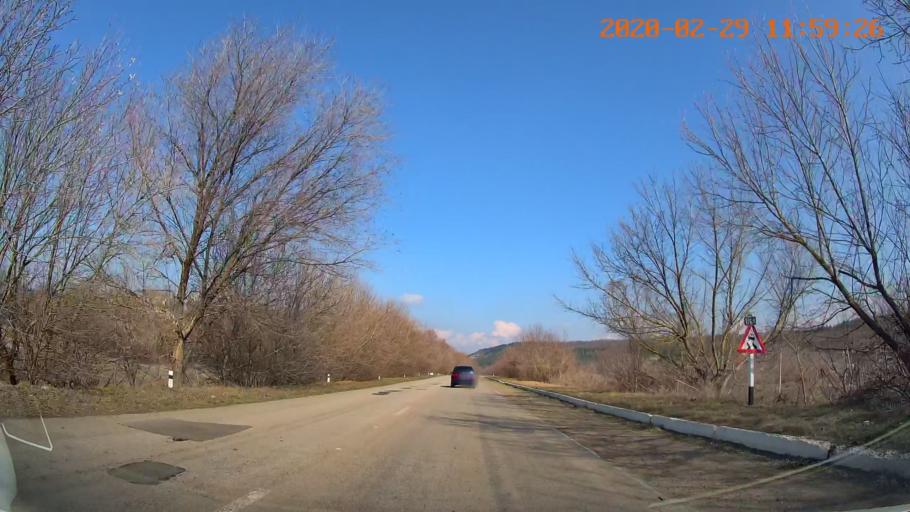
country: MD
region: Telenesti
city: Ribnita
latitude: 47.8251
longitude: 29.0171
